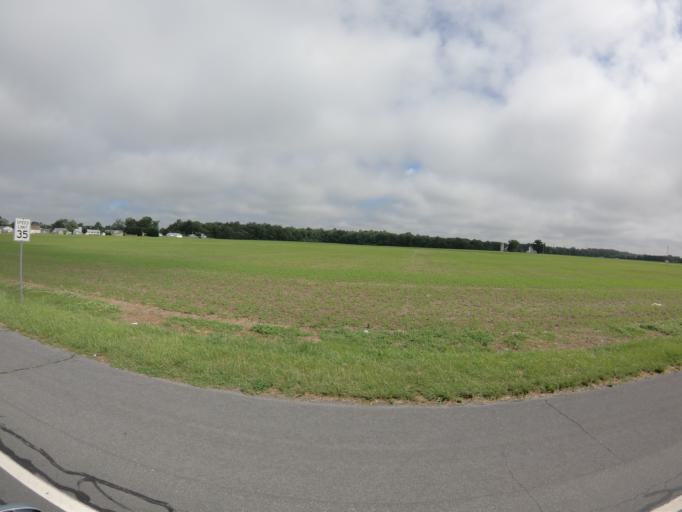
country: US
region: Delaware
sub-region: Kent County
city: Felton
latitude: 39.0061
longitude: -75.5640
